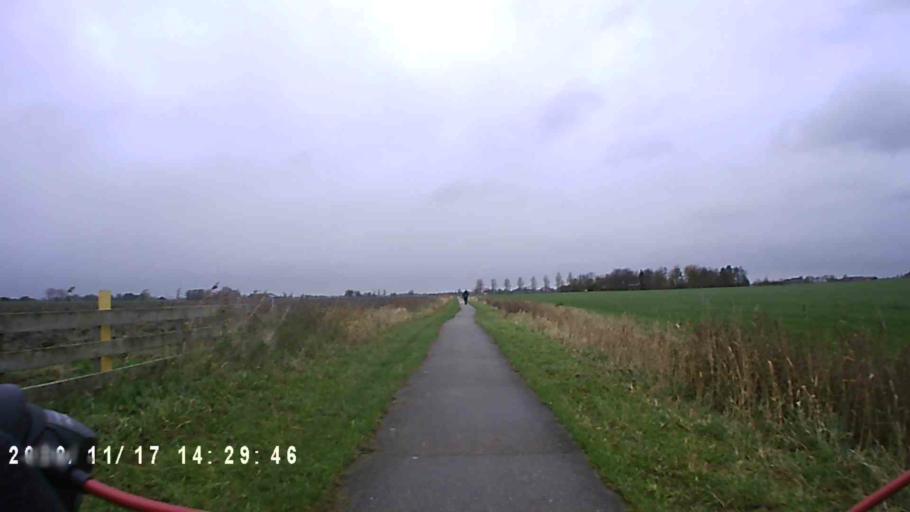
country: NL
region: Groningen
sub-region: Gemeente Zuidhorn
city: Grijpskerk
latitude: 53.2754
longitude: 6.3521
